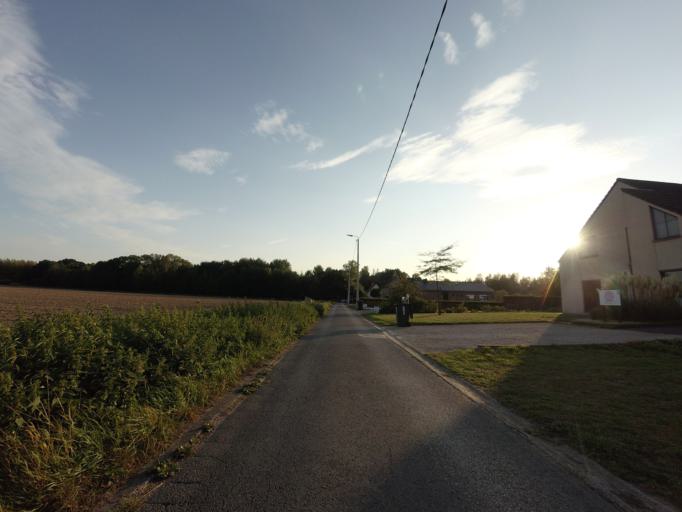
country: BE
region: Flanders
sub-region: Provincie Vlaams-Brabant
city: Kampenhout
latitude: 50.9535
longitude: 4.5742
